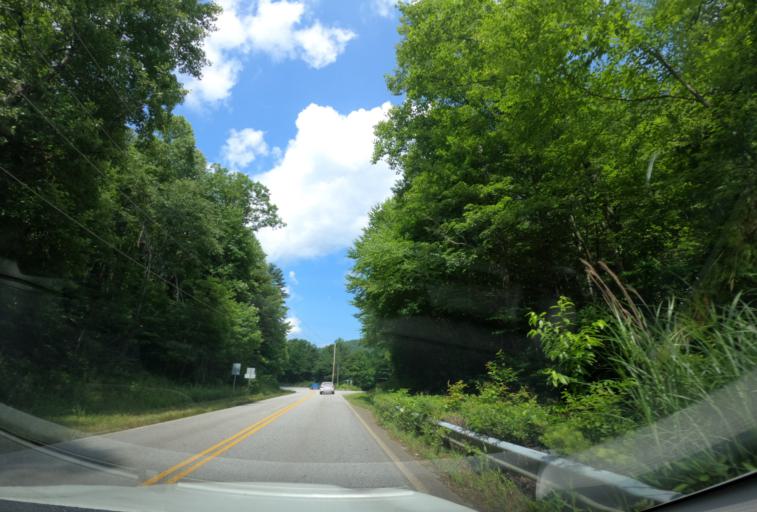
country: US
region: North Carolina
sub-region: Jackson County
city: Cullowhee
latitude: 35.0779
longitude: -82.9942
